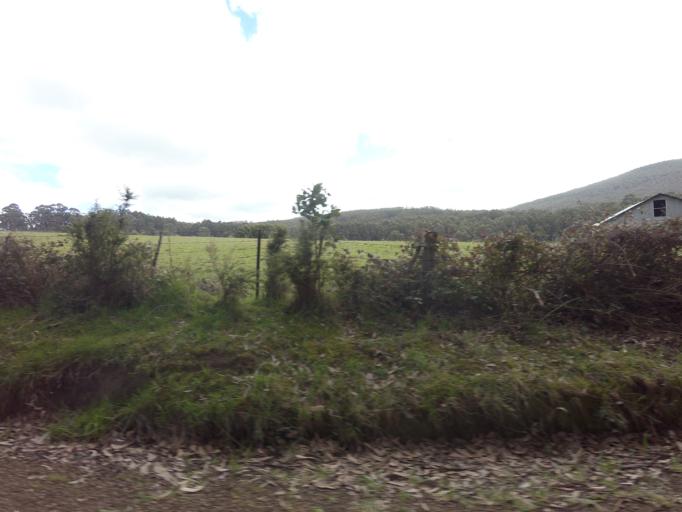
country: AU
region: Tasmania
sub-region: Huon Valley
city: Cygnet
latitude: -43.4109
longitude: 147.0189
